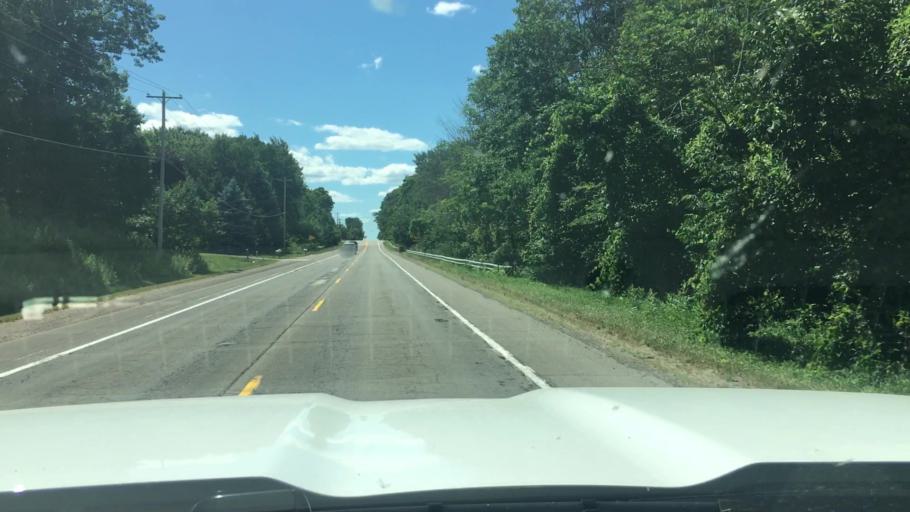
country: US
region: Michigan
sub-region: Kent County
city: Sparta
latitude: 43.1607
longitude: -85.6354
